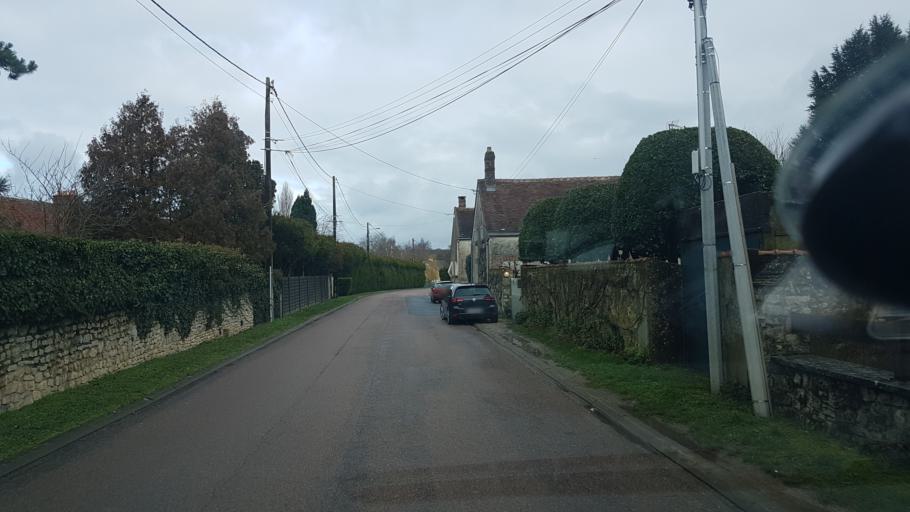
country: FR
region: Ile-de-France
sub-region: Departement de Seine-et-Marne
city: Souppes-sur-Loing
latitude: 48.2242
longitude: 2.7976
